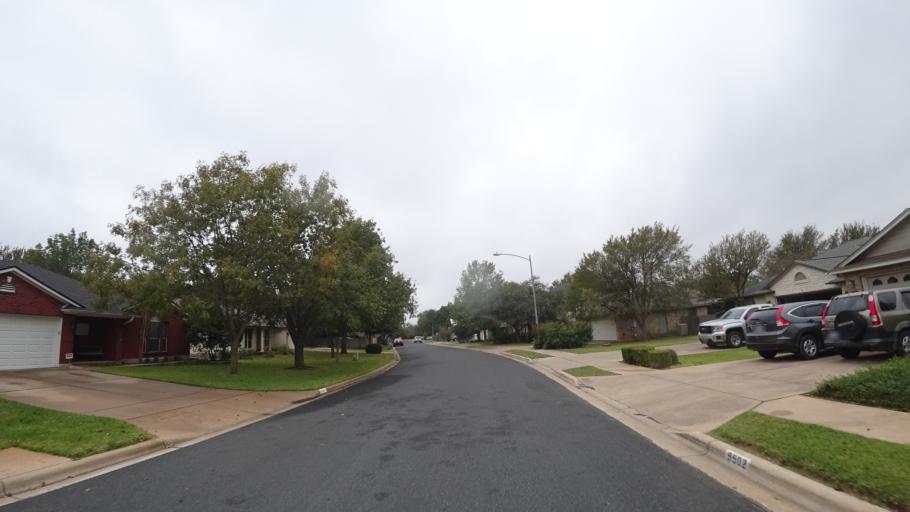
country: US
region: Texas
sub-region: Travis County
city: Shady Hollow
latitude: 30.1883
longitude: -97.8435
